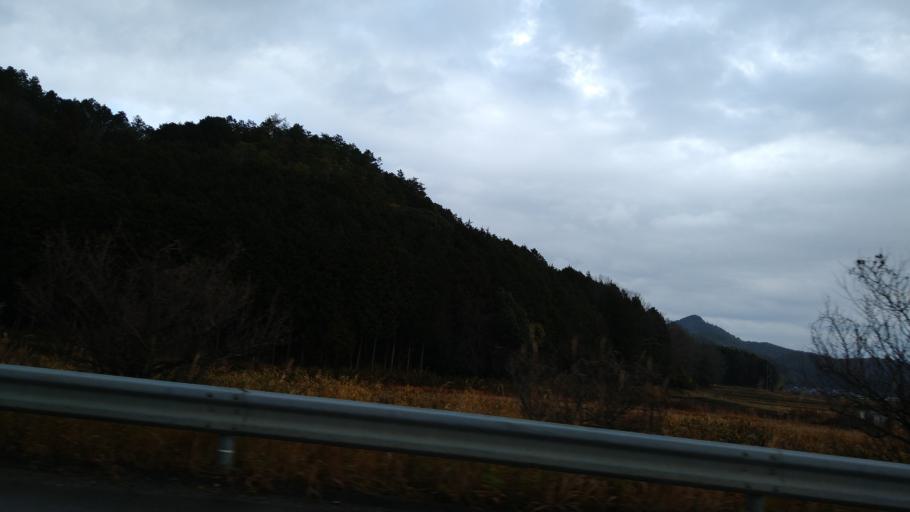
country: JP
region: Kyoto
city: Kameoka
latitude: 35.0532
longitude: 135.4707
